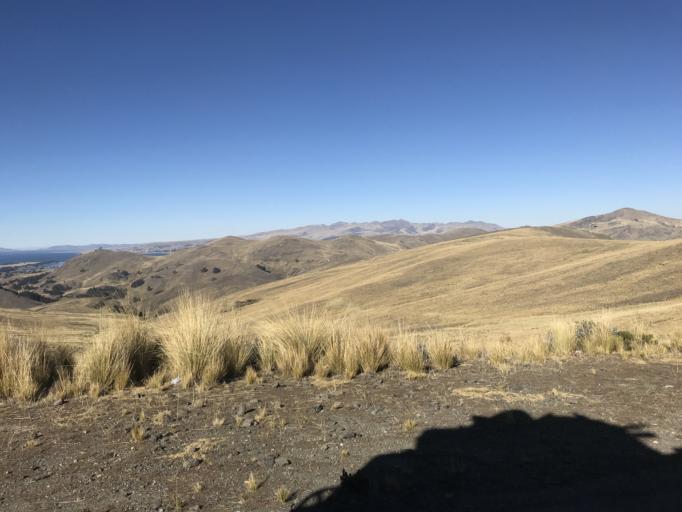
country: PE
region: Puno
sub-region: Yunguyo
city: Yunguyo
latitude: -16.1635
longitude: -68.9872
